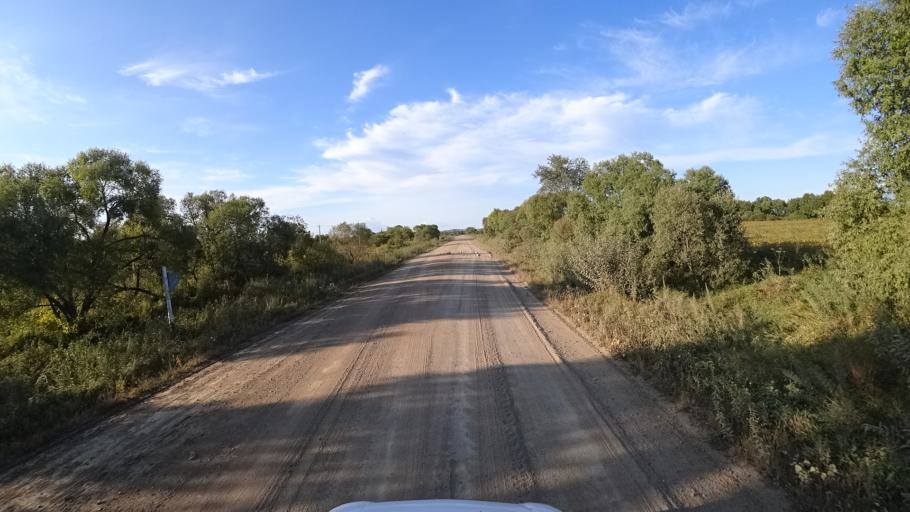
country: RU
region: Amur
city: Arkhara
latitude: 49.3566
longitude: 130.1374
